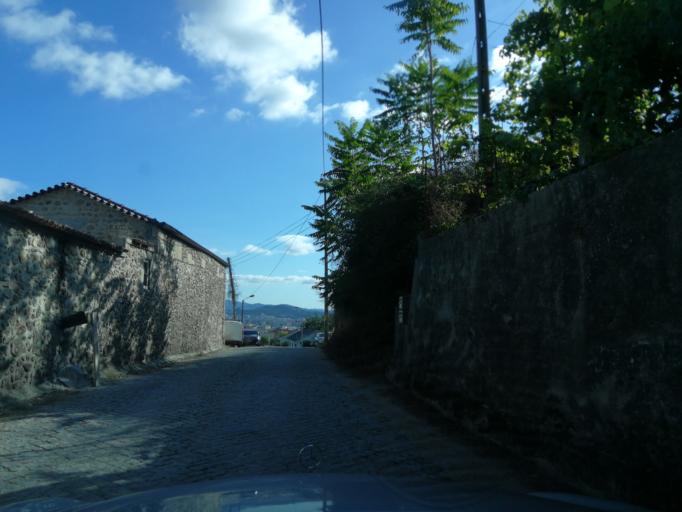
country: PT
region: Braga
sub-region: Braga
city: Adaufe
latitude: 41.5721
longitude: -8.3835
